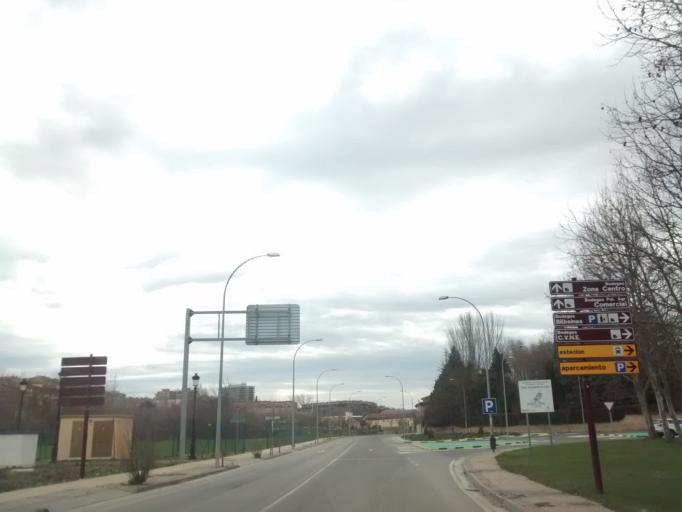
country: ES
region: La Rioja
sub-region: Provincia de La Rioja
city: Haro
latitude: 42.5816
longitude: -2.8471
